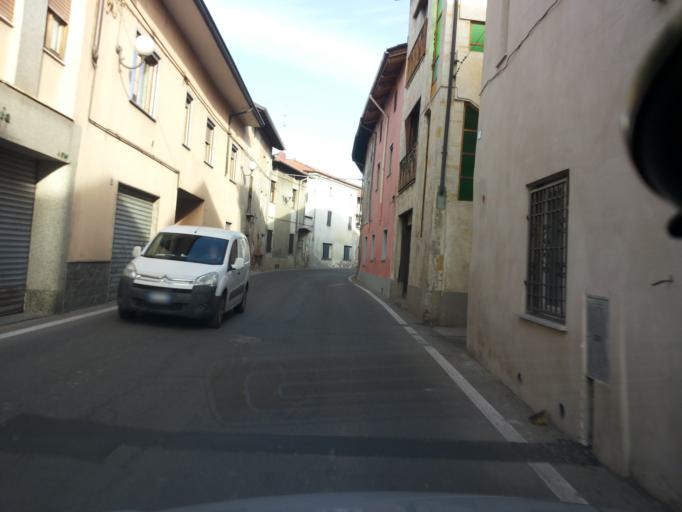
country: IT
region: Piedmont
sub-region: Provincia di Vercelli
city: Ghislarengo
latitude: 45.5272
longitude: 8.3861
